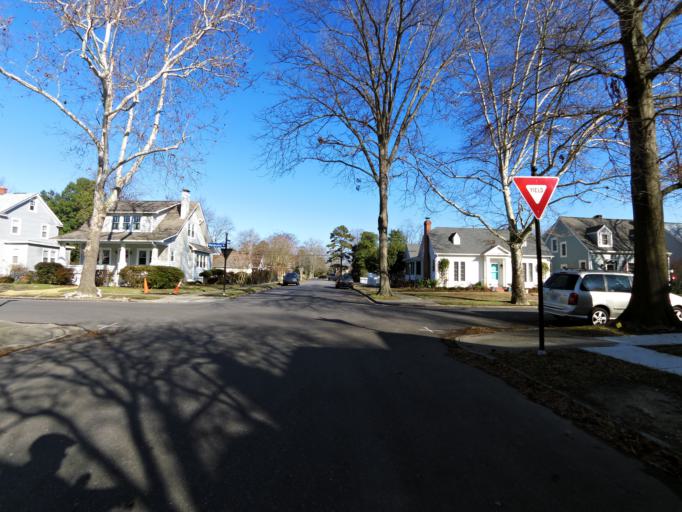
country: US
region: Virginia
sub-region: City of Hampton
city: Hampton
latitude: 37.0018
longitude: -76.3767
